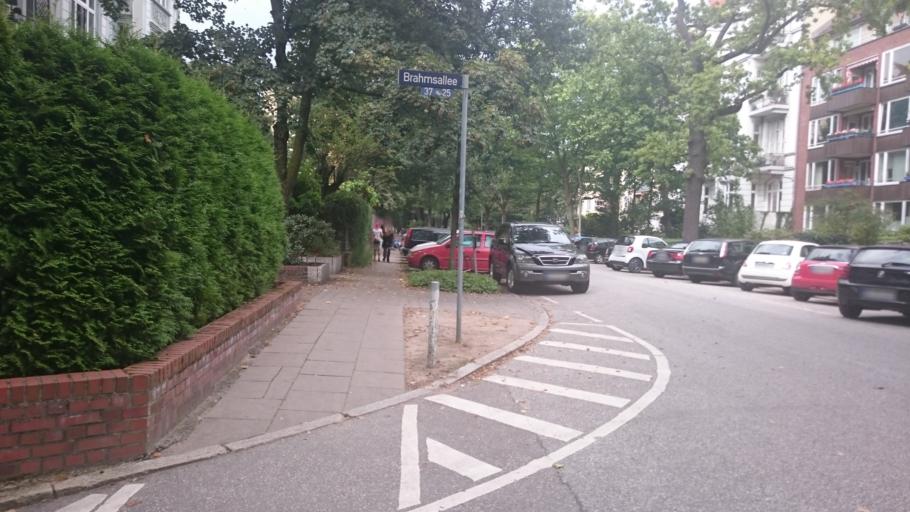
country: DE
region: Hamburg
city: Eimsbuettel
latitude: 53.5745
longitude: 9.9817
